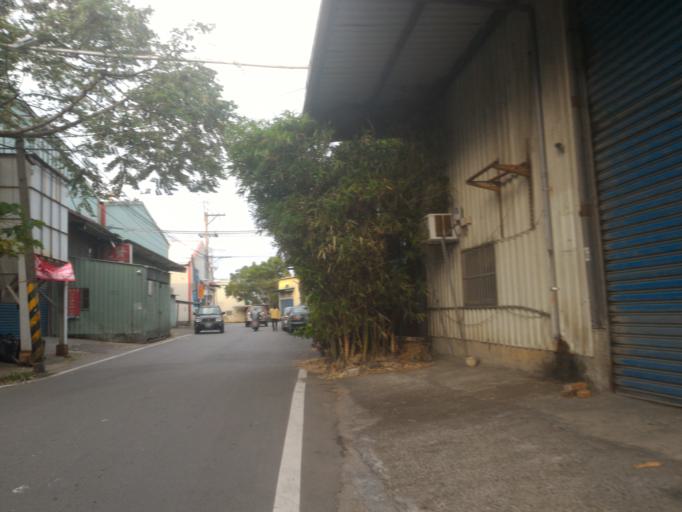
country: TW
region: Taipei
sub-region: Taipei
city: Banqiao
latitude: 24.9543
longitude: 121.4055
